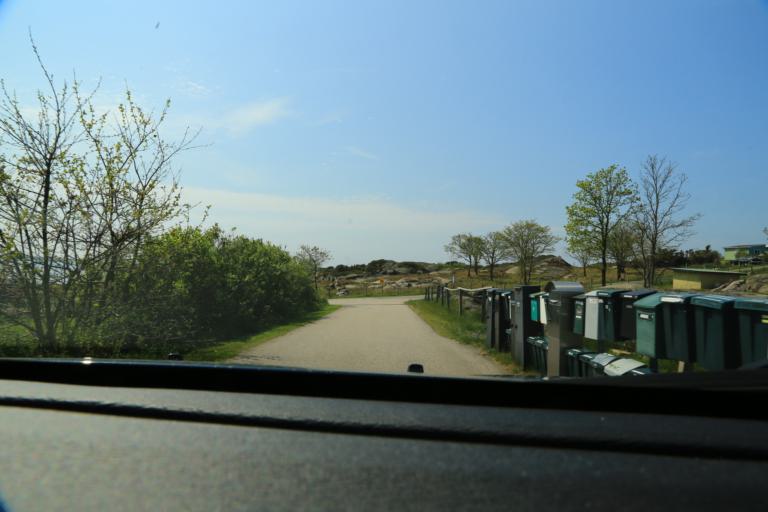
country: SE
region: Halland
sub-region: Varbergs Kommun
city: Varberg
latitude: 57.1417
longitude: 12.2193
